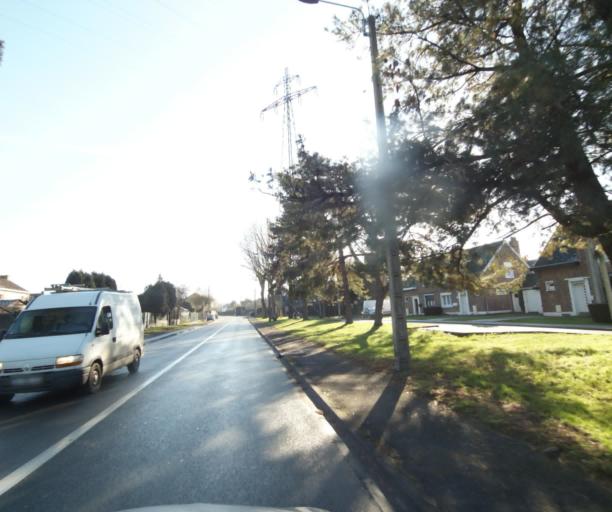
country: FR
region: Nord-Pas-de-Calais
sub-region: Departement du Nord
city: Marly
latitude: 50.3404
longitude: 3.5503
